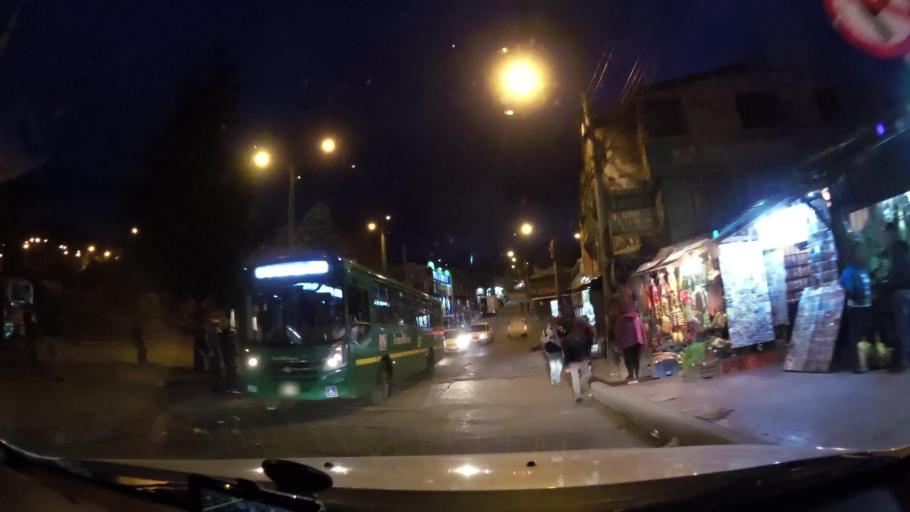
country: CO
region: Bogota D.C.
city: Bogota
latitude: 4.5494
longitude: -74.0925
